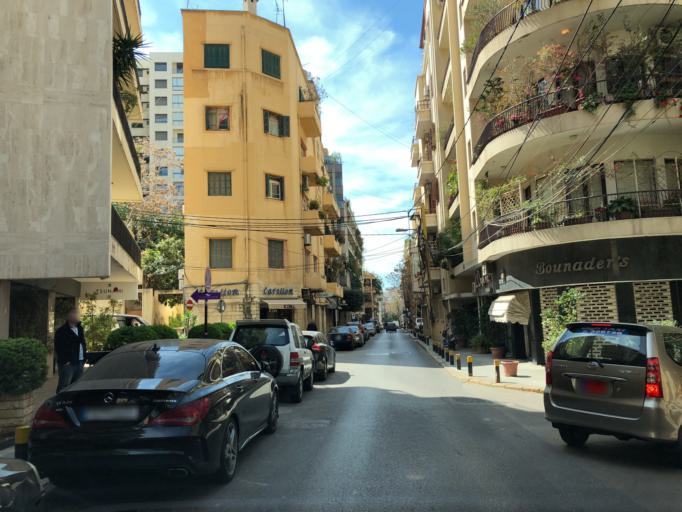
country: LB
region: Beyrouth
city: Beirut
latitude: 33.8885
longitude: 35.5147
